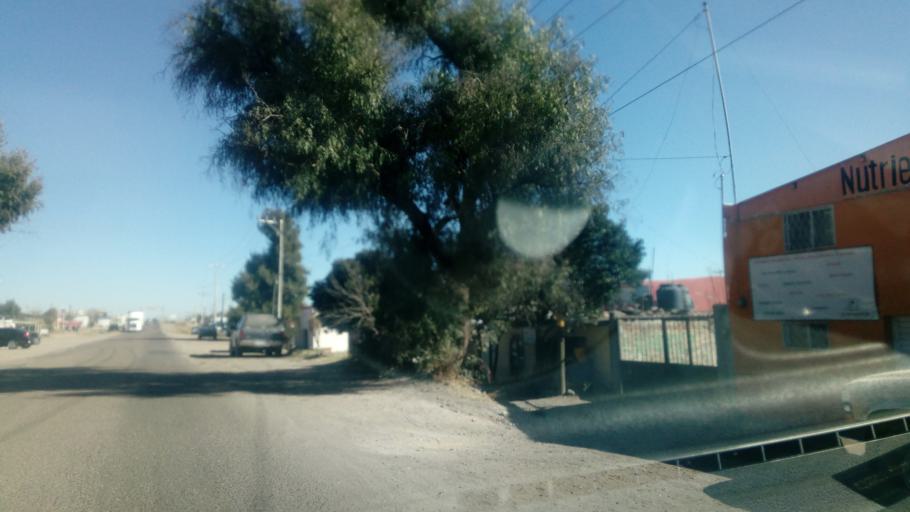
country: MX
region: Durango
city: Victoria de Durango
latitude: 24.1029
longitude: -104.5743
